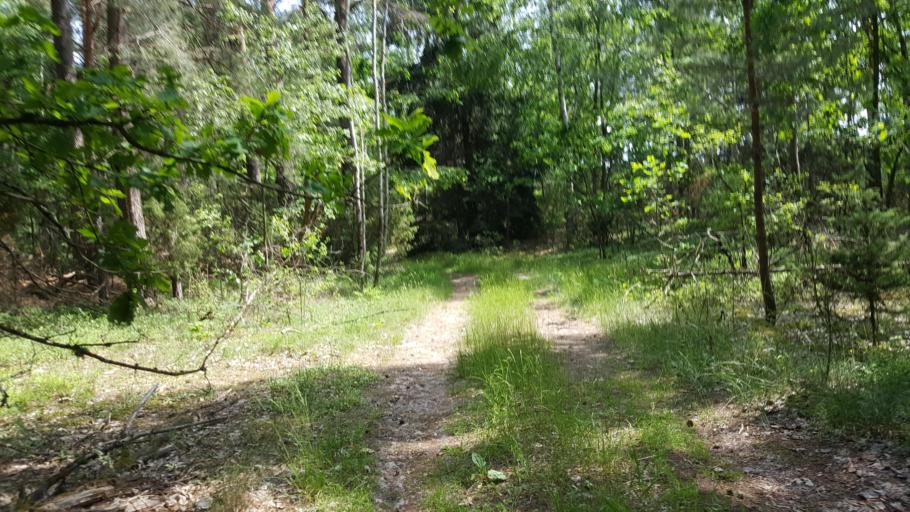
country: BY
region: Brest
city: Kamyanyuki
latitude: 52.5031
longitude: 23.8349
